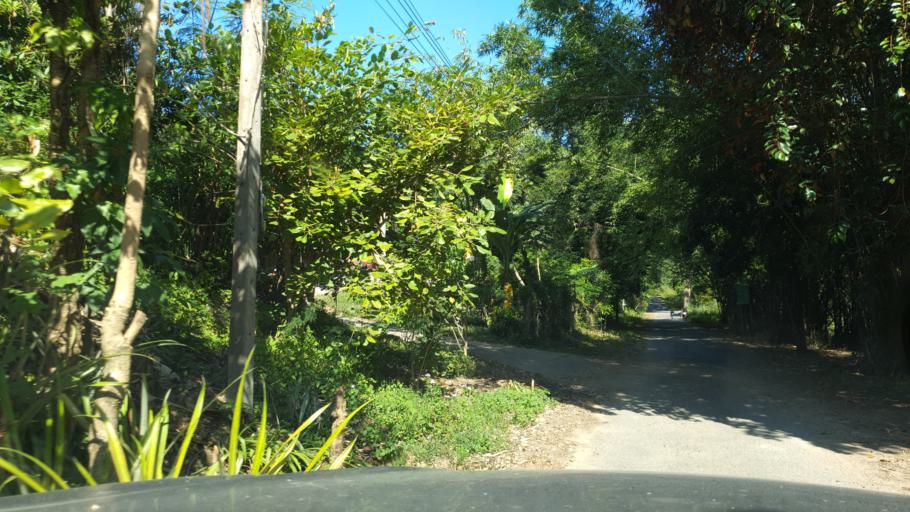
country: TH
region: Chiang Mai
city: San Sai
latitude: 18.8897
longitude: 99.1680
